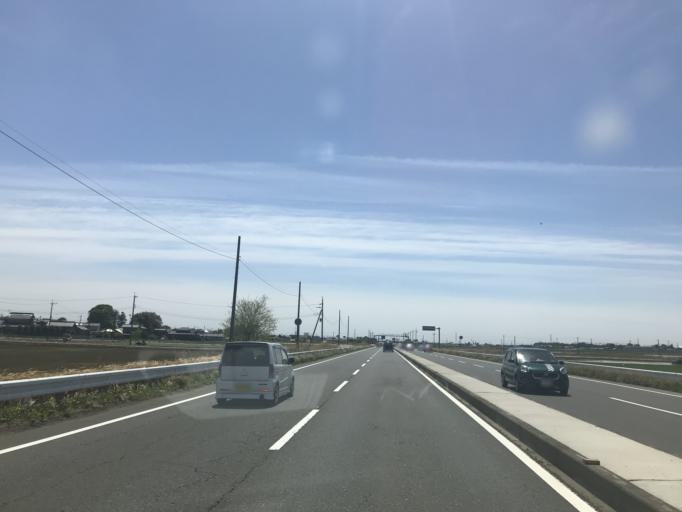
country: JP
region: Ibaraki
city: Shimodate
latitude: 36.2108
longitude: 139.9852
